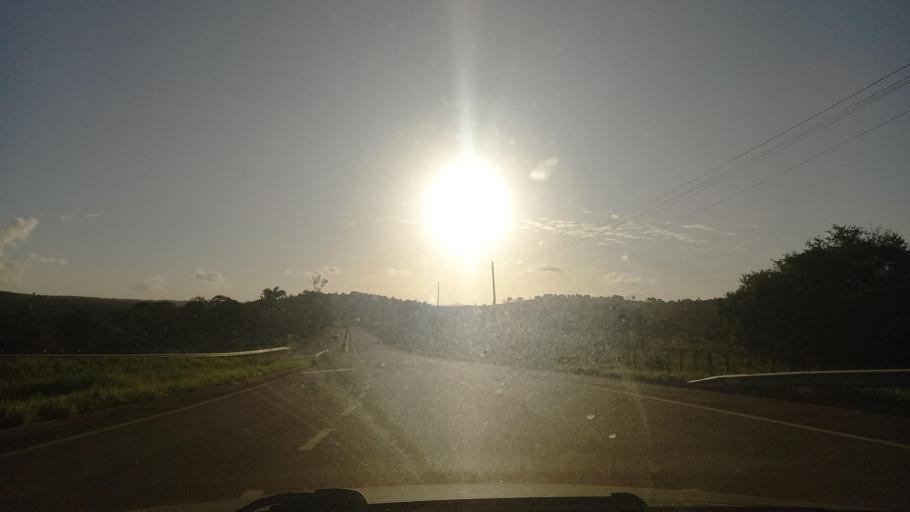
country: BR
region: Alagoas
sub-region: Limoeiro De Anadia
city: Limoeiro de Anadia
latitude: -9.7383
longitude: -36.4861
